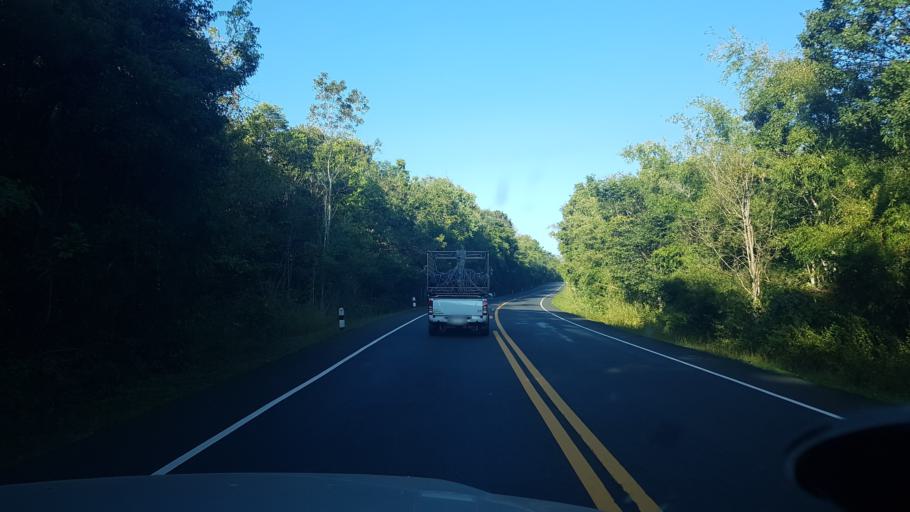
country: TH
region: Phetchabun
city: Nam Nao
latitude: 16.7014
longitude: 101.6153
